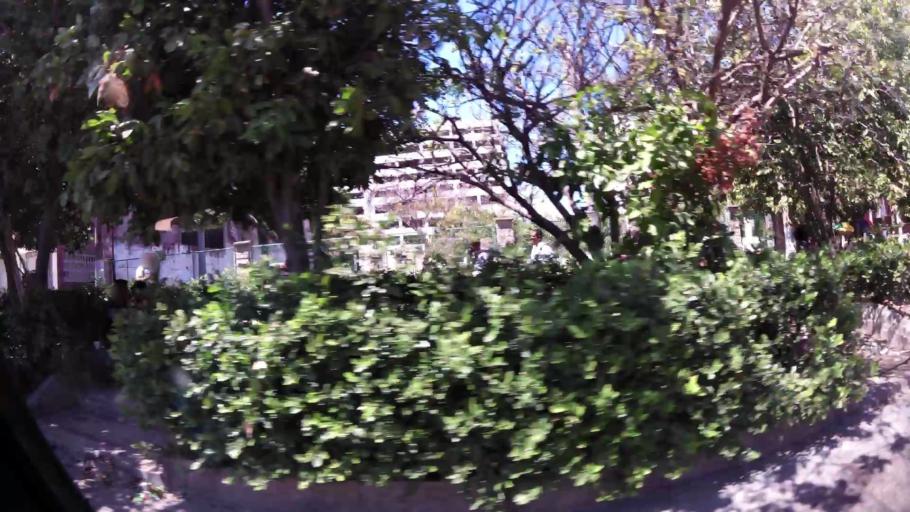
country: CO
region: Atlantico
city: Barranquilla
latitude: 10.9945
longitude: -74.8028
